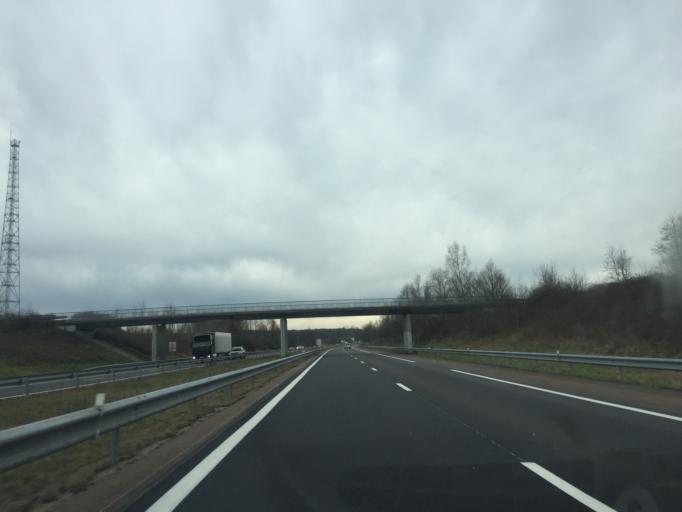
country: FR
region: Franche-Comte
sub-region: Departement du Jura
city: Bletterans
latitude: 46.8050
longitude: 5.5331
